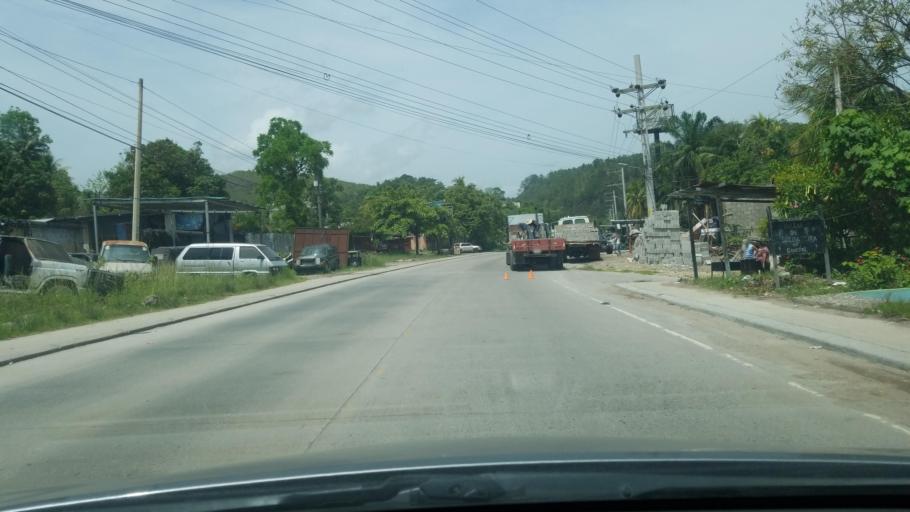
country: HN
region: Copan
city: La Entrada
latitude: 15.0493
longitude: -88.7573
